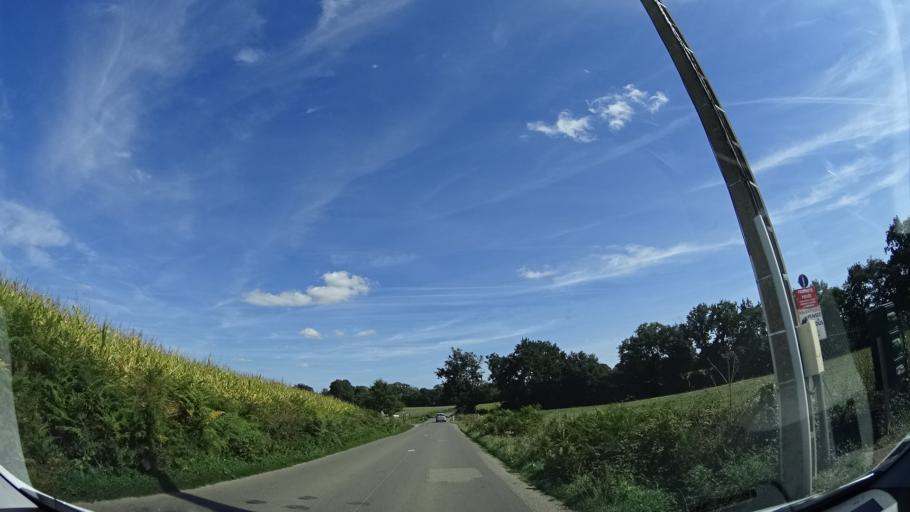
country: FR
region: Brittany
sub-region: Departement d'Ille-et-Vilaine
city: Saint-Sulpice-la-Foret
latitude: 48.2188
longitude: -1.5687
